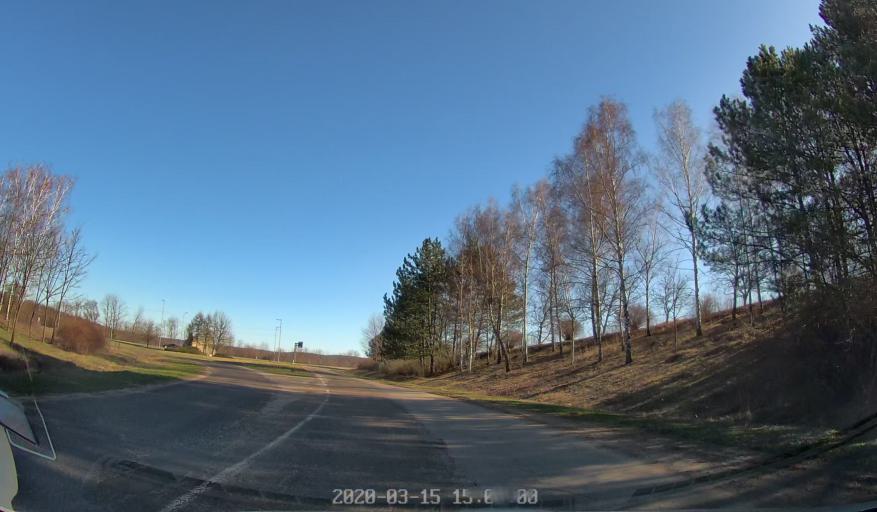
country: MD
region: Orhei
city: Orhei
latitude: 47.2914
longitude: 28.8056
